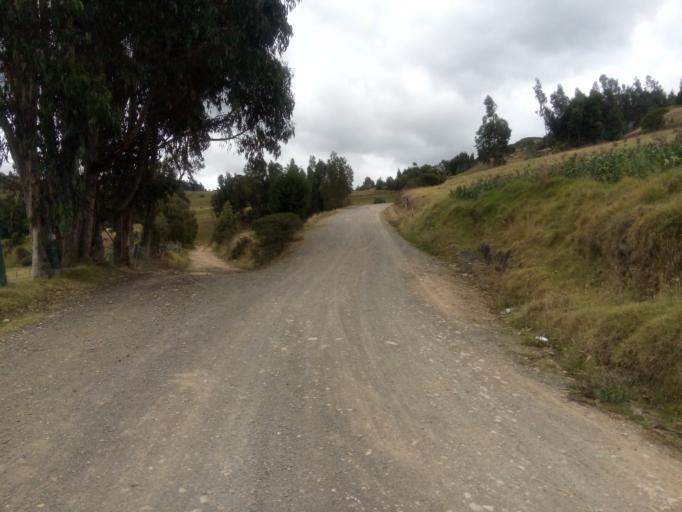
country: CO
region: Boyaca
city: Gameza
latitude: 5.8171
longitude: -72.8033
